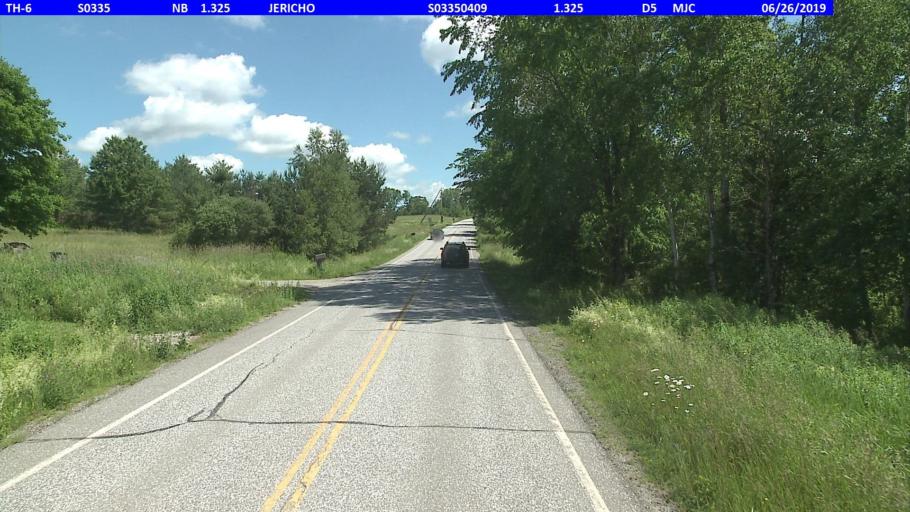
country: US
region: Vermont
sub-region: Chittenden County
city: Jericho
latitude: 44.4833
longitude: -73.0160
